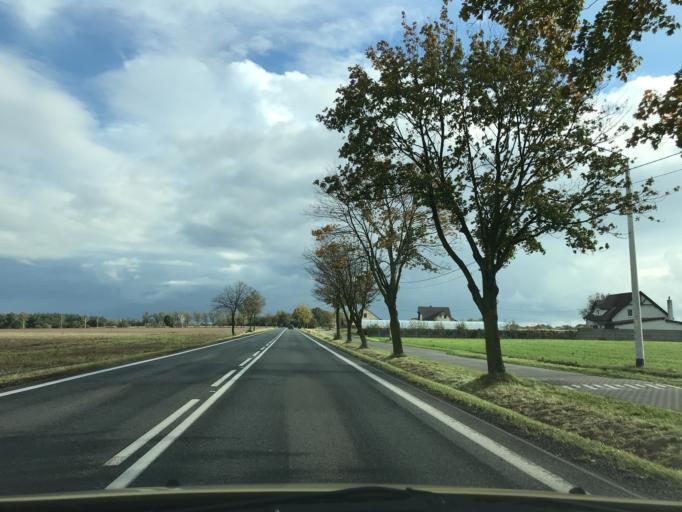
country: PL
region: Greater Poland Voivodeship
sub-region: Powiat ostrowski
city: Nowe Skalmierzyce
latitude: 51.7806
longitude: 18.0144
